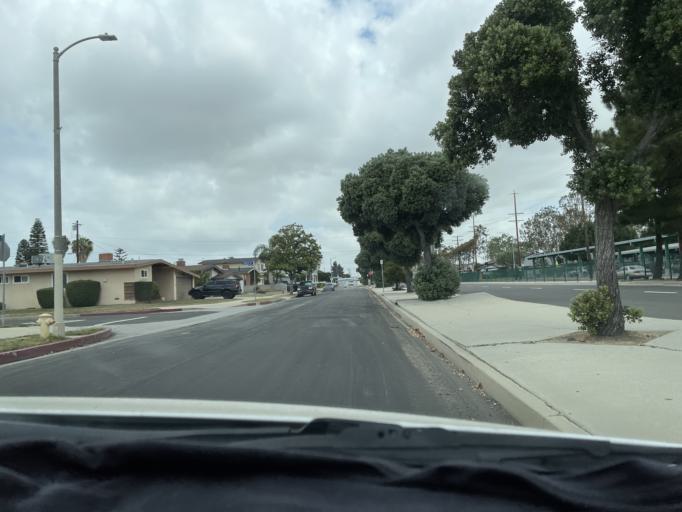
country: US
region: California
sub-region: Los Angeles County
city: Lomita
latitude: 33.8038
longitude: -118.3076
